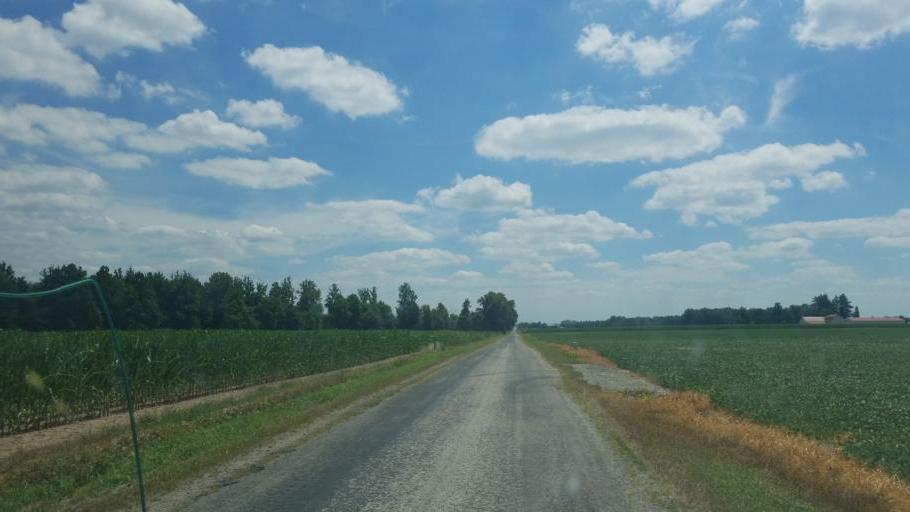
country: US
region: Ohio
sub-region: Defiance County
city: Hicksville
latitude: 41.3503
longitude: -84.6901
